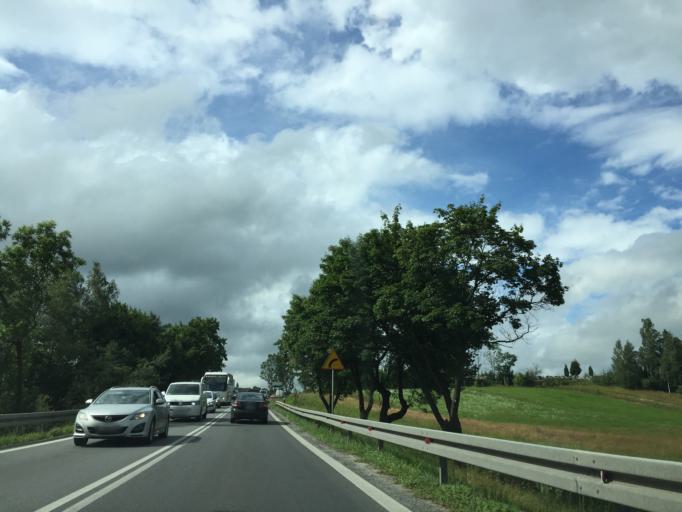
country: PL
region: Lesser Poland Voivodeship
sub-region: Powiat nowotarski
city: Lasek
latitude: 49.5105
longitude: 19.9892
